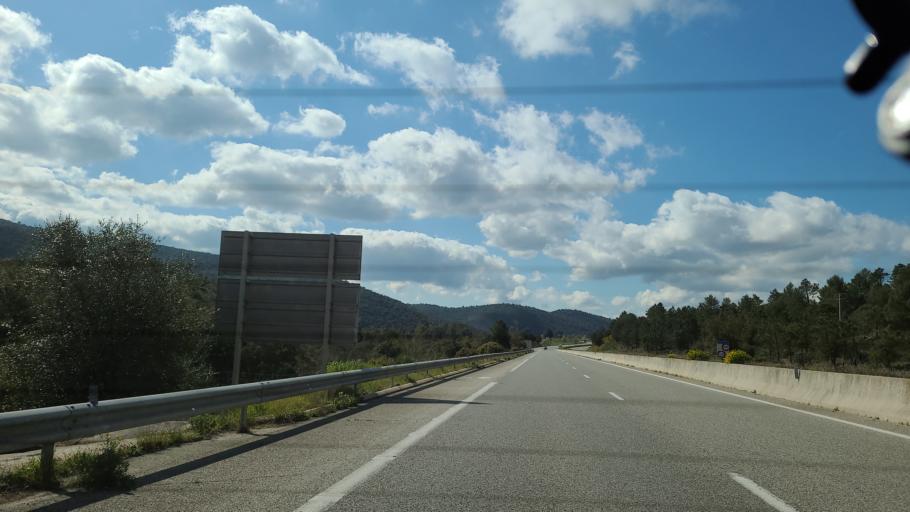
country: FR
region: Provence-Alpes-Cote d'Azur
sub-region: Departement du Var
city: Carnoules
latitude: 43.2804
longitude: 6.1879
